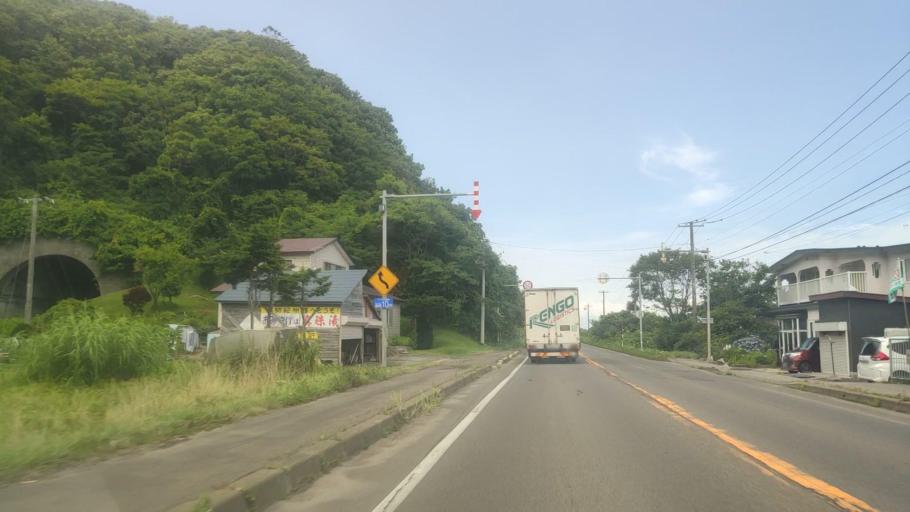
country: JP
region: Hokkaido
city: Nanae
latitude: 42.1615
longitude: 140.4704
